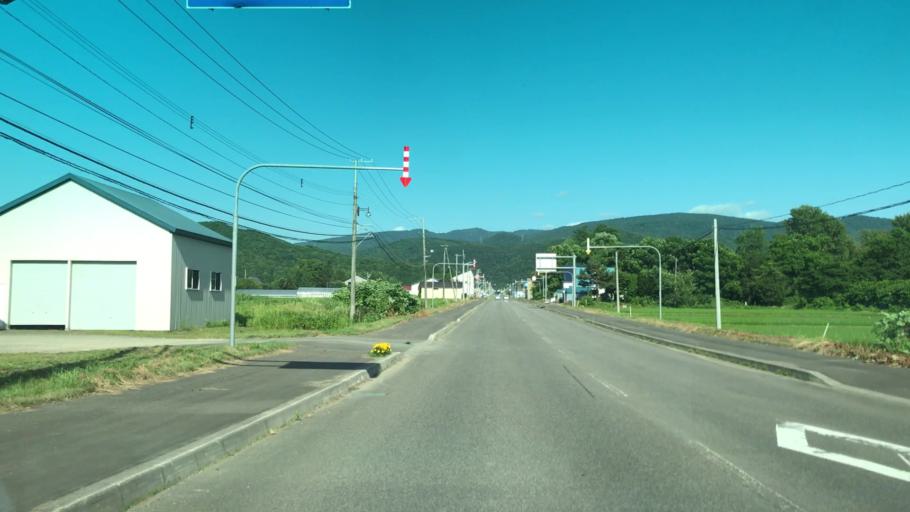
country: JP
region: Hokkaido
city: Yoichi
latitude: 43.0509
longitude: 140.8262
